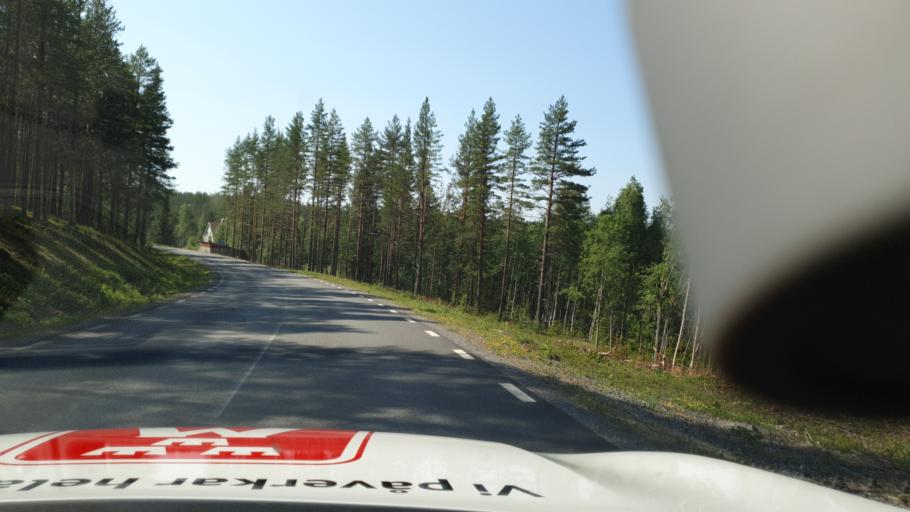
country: SE
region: Vaesterbotten
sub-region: Skelleftea Kommun
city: Langsele
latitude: 64.9501
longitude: 20.0240
